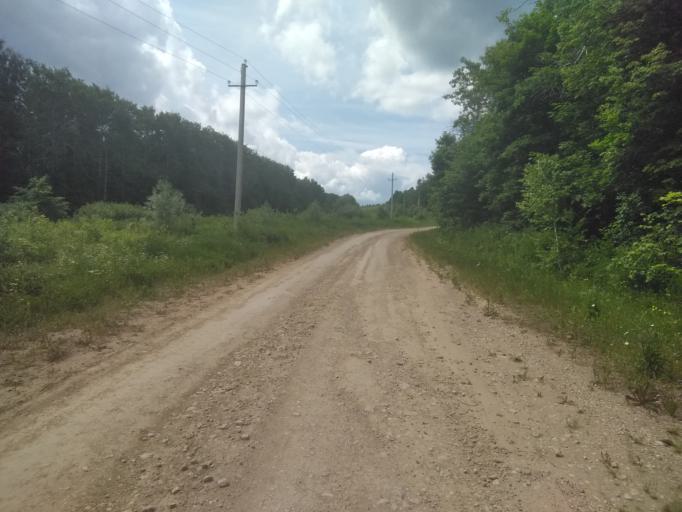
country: RU
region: Chelyabinsk
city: Sim
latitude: 54.9988
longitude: 57.5161
